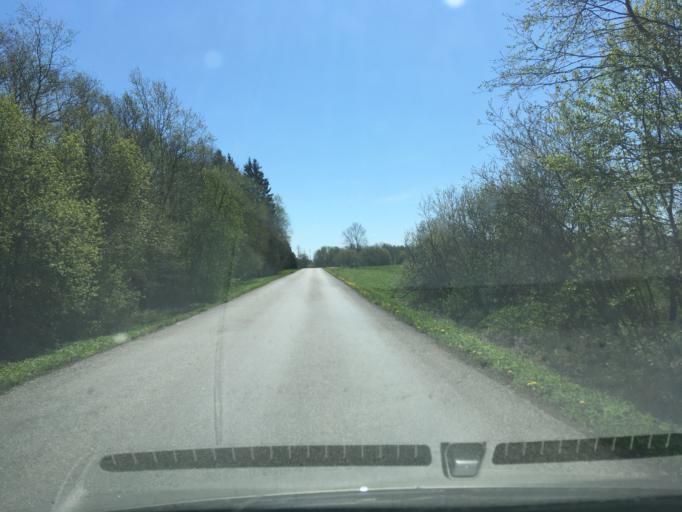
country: EE
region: Harju
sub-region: Raasiku vald
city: Arukula
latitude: 59.4078
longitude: 25.0774
